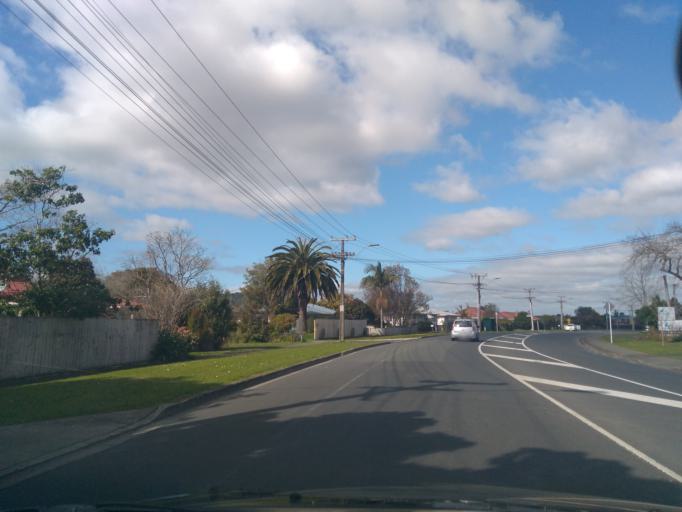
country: NZ
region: Northland
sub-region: Whangarei
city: Whangarei
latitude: -35.6915
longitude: 174.3272
